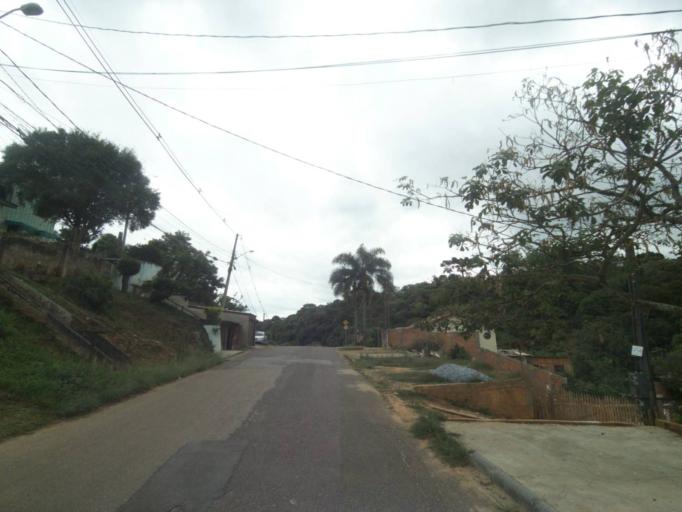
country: BR
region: Parana
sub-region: Curitiba
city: Curitiba
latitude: -25.3869
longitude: -49.2941
